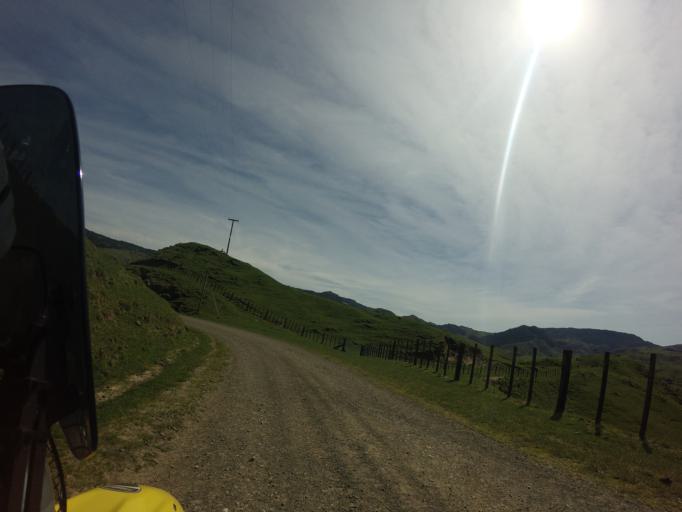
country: NZ
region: Bay of Plenty
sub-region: Opotiki District
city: Opotiki
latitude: -38.4532
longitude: 177.3574
